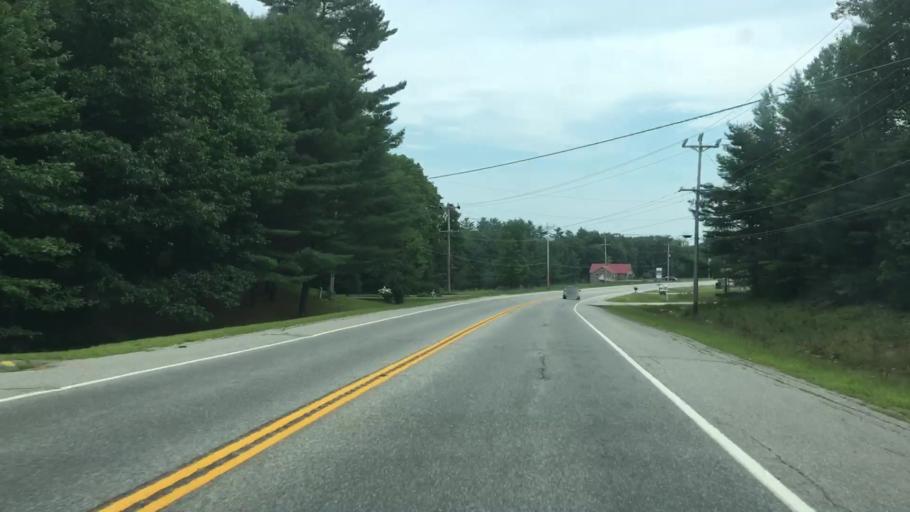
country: US
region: Maine
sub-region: Oxford County
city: Bethel
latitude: 44.4332
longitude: -70.8025
